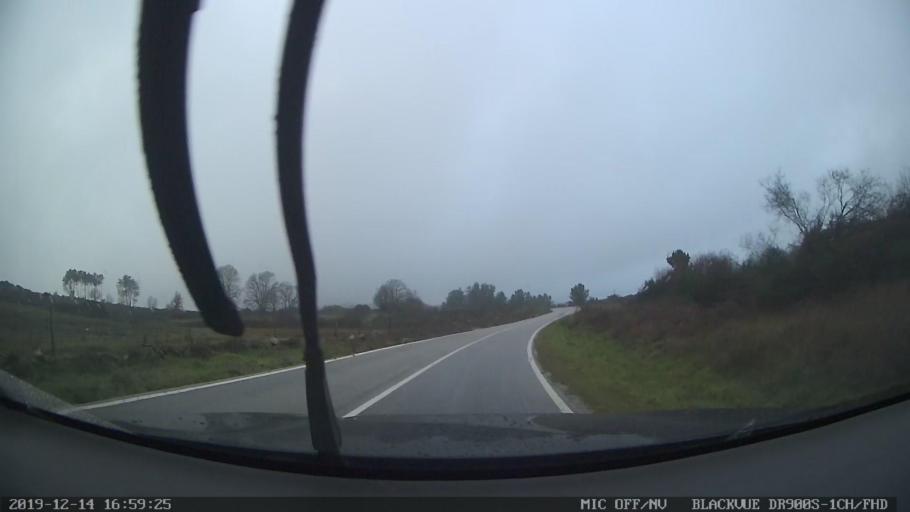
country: PT
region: Vila Real
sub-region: Vila Pouca de Aguiar
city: Vila Pouca de Aguiar
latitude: 41.4359
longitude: -7.5624
